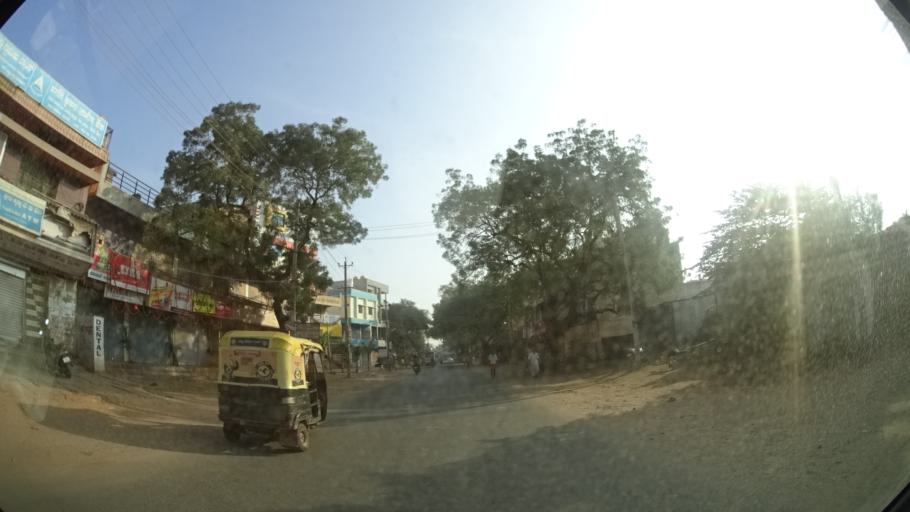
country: IN
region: Karnataka
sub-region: Bellary
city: Hospet
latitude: 15.2659
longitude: 76.3870
